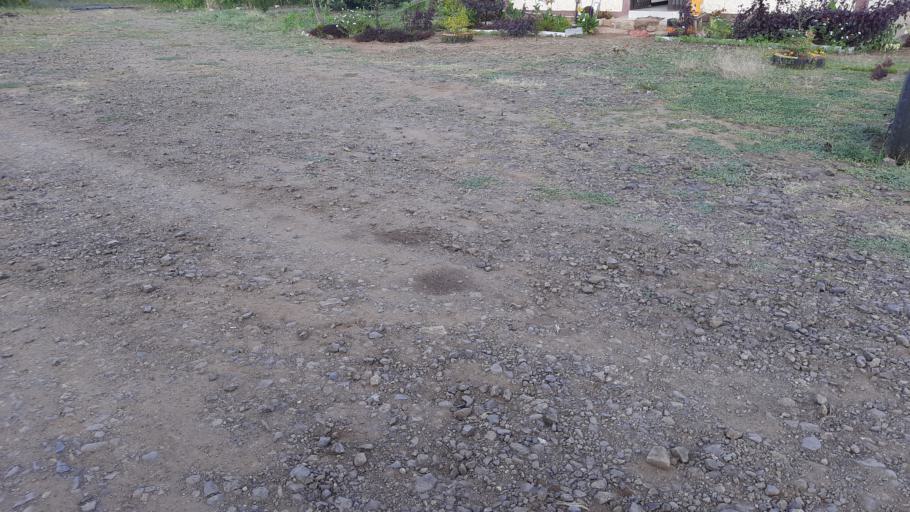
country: ET
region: Oromiya
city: Hagere Maryam
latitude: 5.8280
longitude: 37.9313
